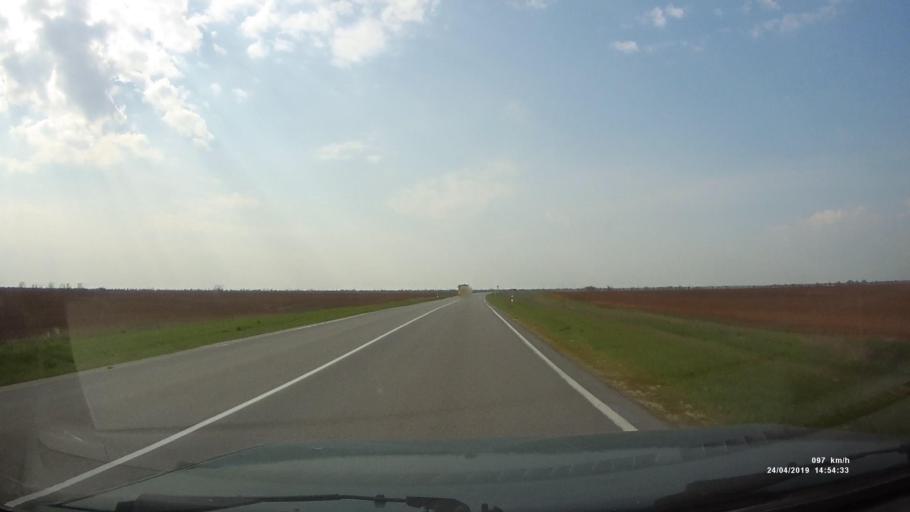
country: RU
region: Rostov
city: Remontnoye
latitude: 46.5352
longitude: 43.6367
